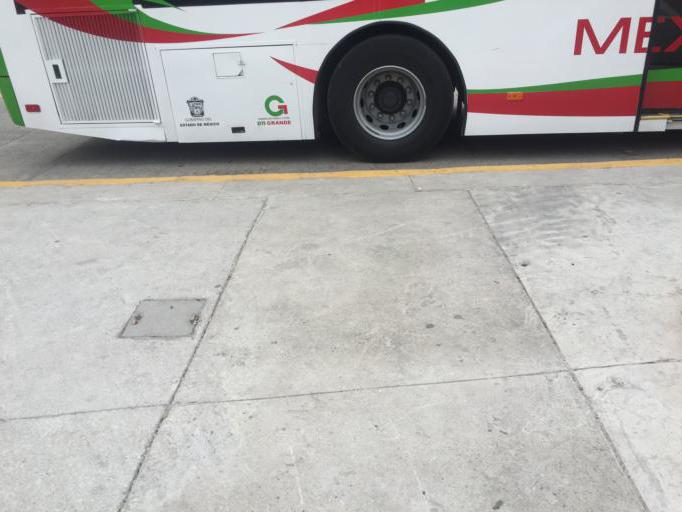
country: MX
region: Mexico
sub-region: Tlalnepantla de Baz
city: Puerto Escondido (Tepeolulco Puerto Escondido)
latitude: 19.5399
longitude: -99.0588
